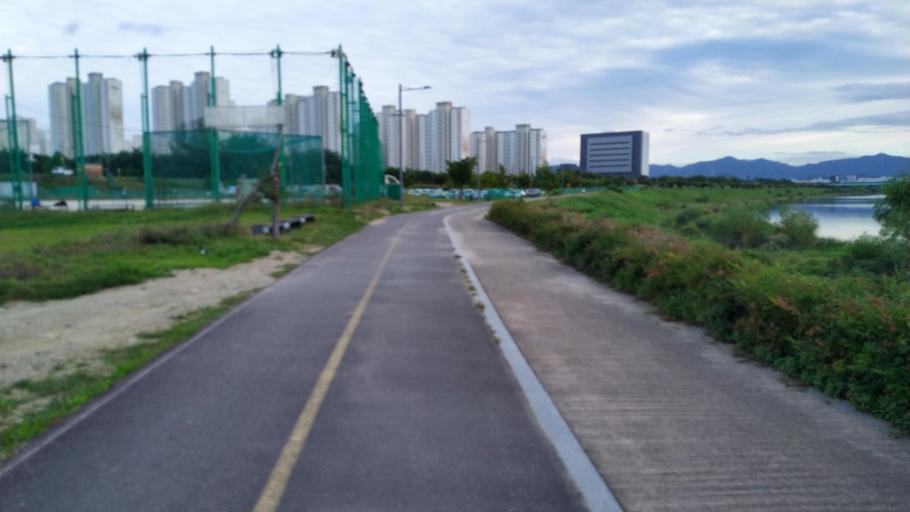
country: KR
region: Daegu
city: Daegu
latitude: 35.9286
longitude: 128.6308
